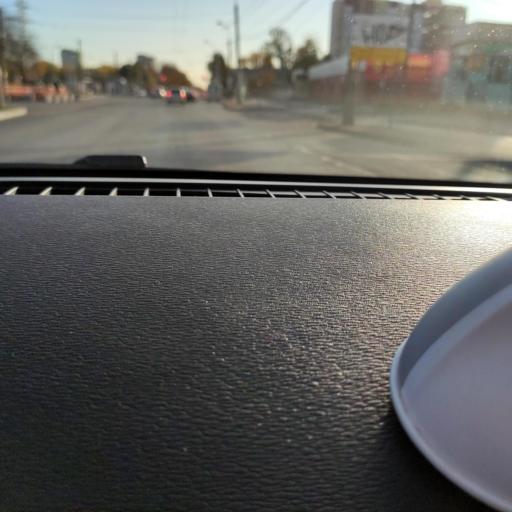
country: RU
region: Samara
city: Samara
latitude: 53.2112
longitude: 50.1999
